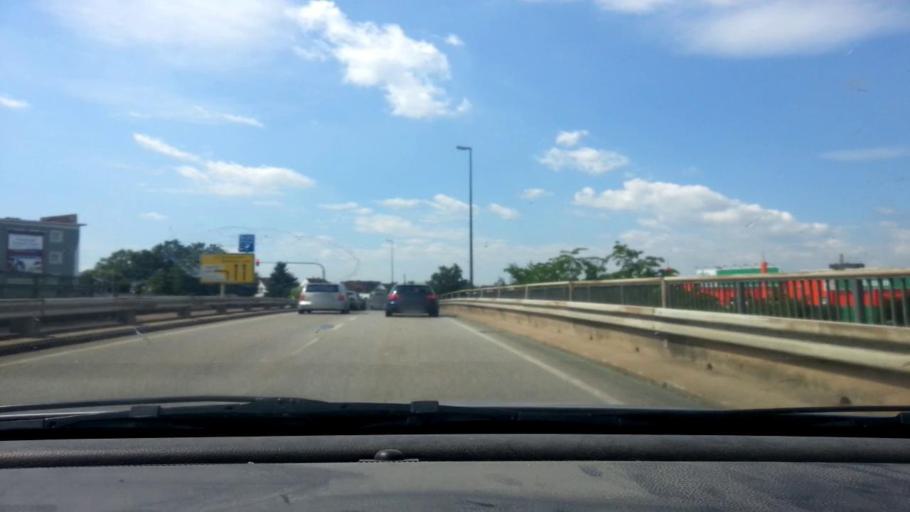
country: DE
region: Bavaria
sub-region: Upper Franconia
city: Bayreuth
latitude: 49.9561
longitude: 11.6030
